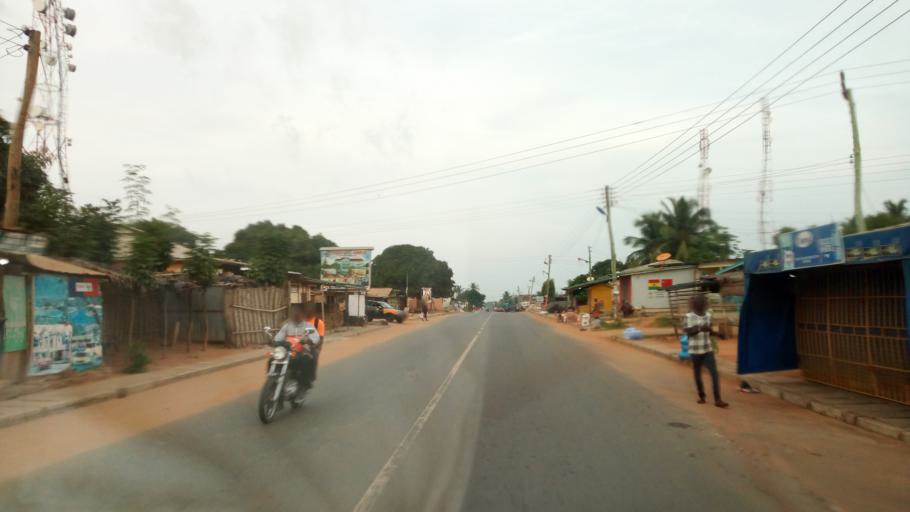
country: GH
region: Volta
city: Keta
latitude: 6.0735
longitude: 1.0351
